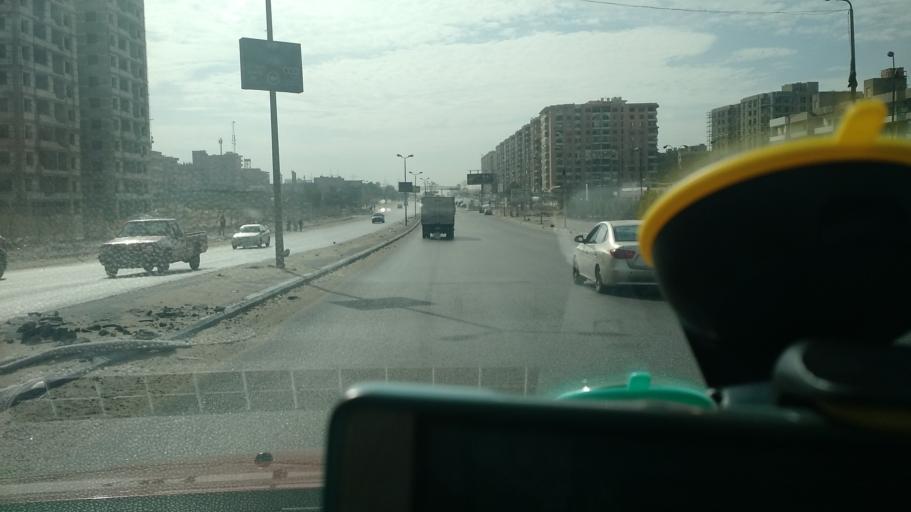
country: EG
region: Al Jizah
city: Al Hawamidiyah
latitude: 29.9612
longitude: 31.2875
